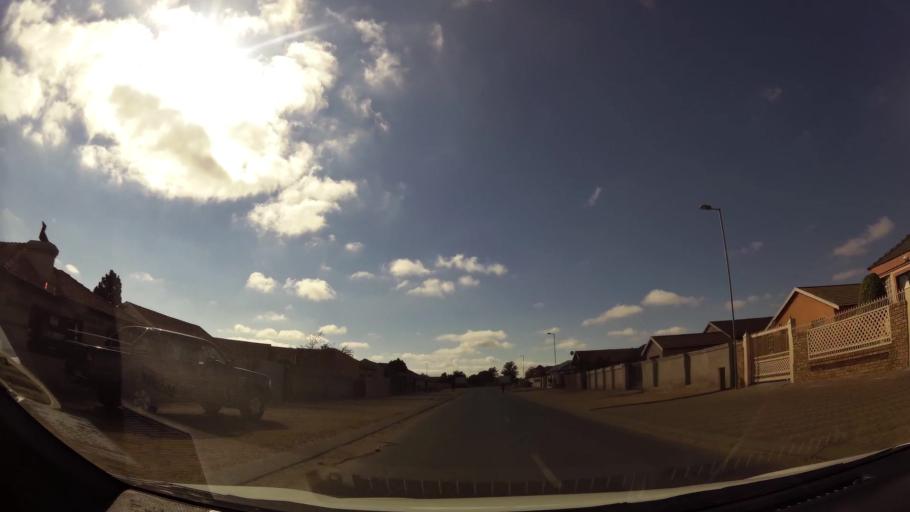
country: ZA
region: Limpopo
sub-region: Capricorn District Municipality
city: Polokwane
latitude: -23.8573
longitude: 29.3738
